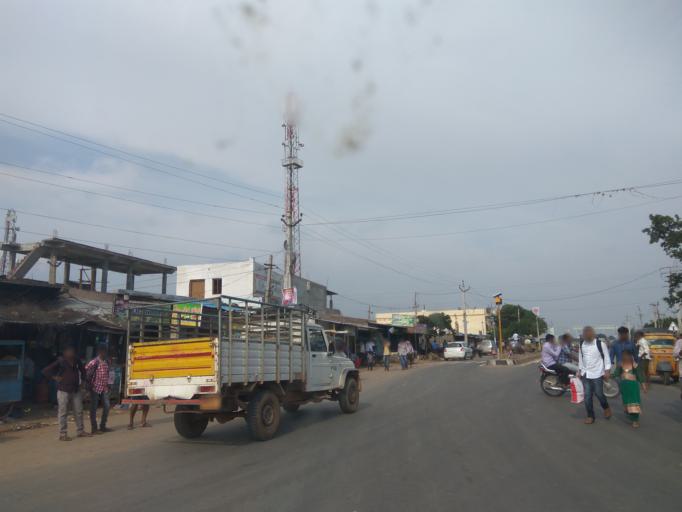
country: IN
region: Andhra Pradesh
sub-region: Prakasam
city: Chemmumiahpet
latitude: 15.9018
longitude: 79.3000
